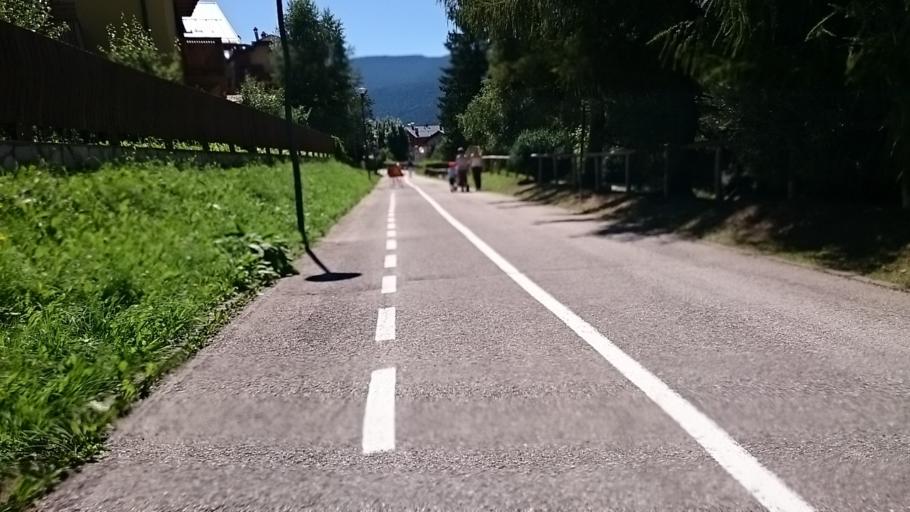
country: IT
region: Veneto
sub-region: Provincia di Belluno
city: San Vito
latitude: 46.4578
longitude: 12.2068
